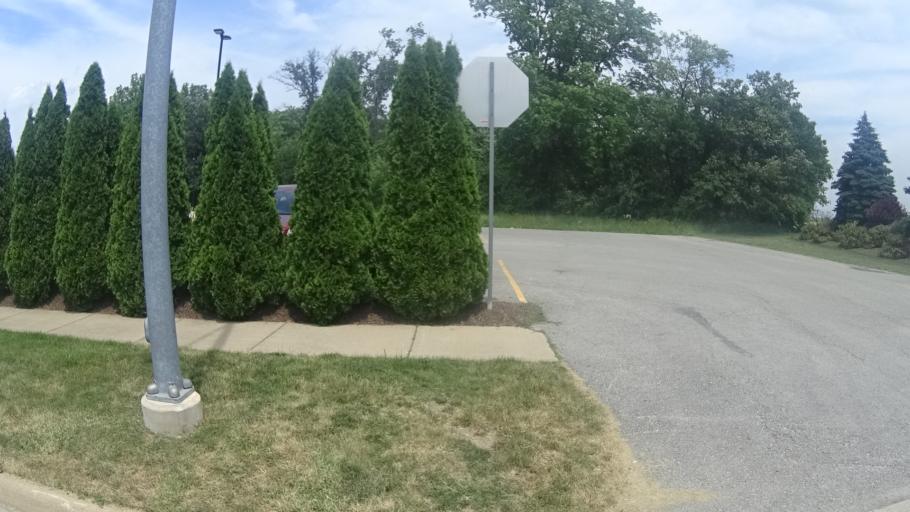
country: US
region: Ohio
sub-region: Erie County
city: Huron
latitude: 41.3824
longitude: -82.6384
